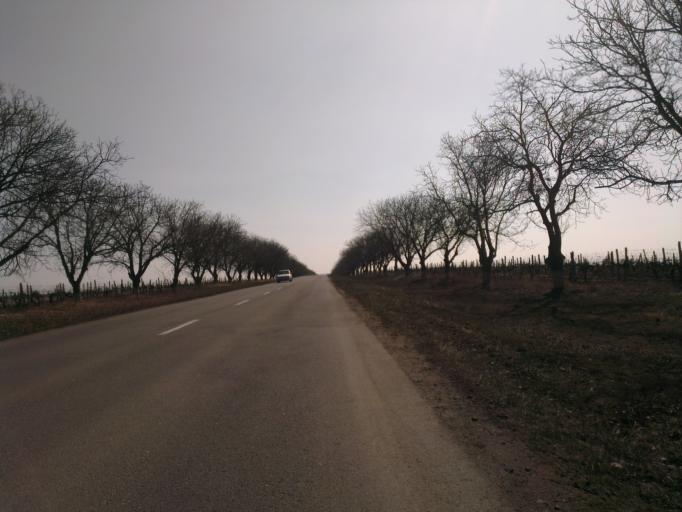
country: MD
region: Chisinau
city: Cricova
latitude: 47.1279
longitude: 28.8544
